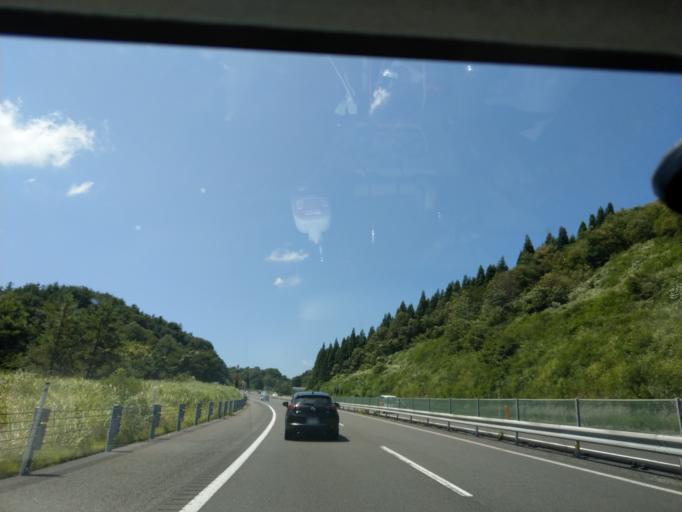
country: JP
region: Akita
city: Akita
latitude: 39.6006
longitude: 140.2752
